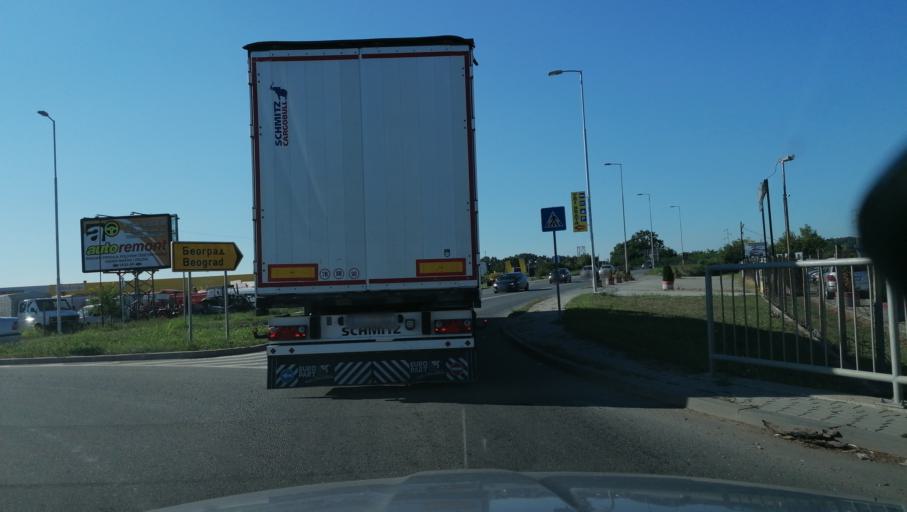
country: RS
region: Central Serbia
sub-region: Raski Okrug
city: Kraljevo
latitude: 43.7426
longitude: 20.6644
